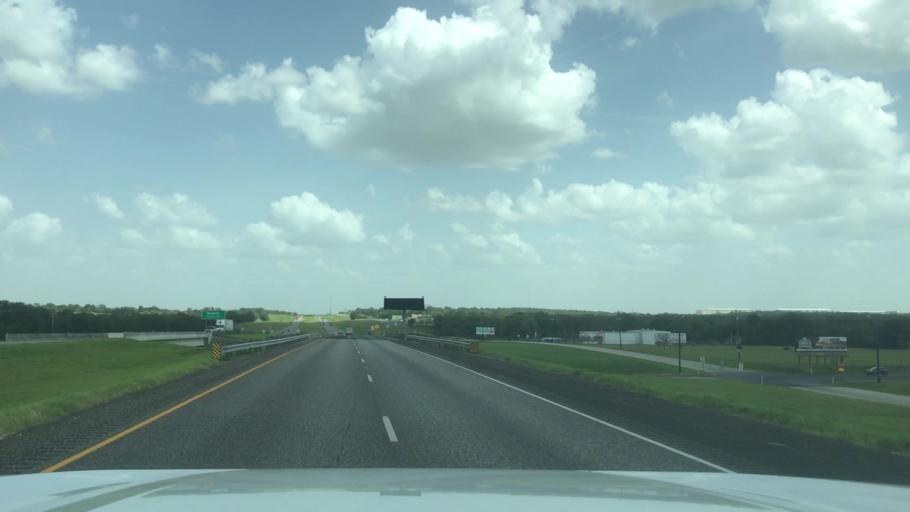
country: US
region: Texas
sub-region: Brazos County
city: Bryan
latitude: 30.7477
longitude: -96.4574
